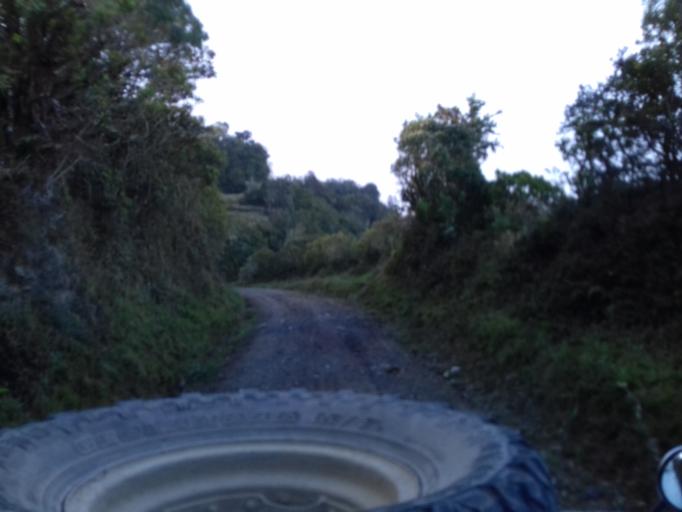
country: CO
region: Quindio
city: Salento
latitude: 4.5636
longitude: -75.5180
